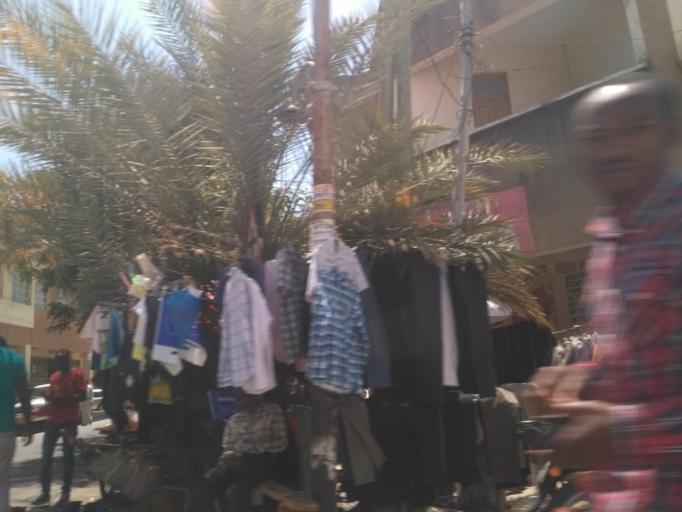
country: TZ
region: Dodoma
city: Dodoma
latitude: -6.1804
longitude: 35.7475
